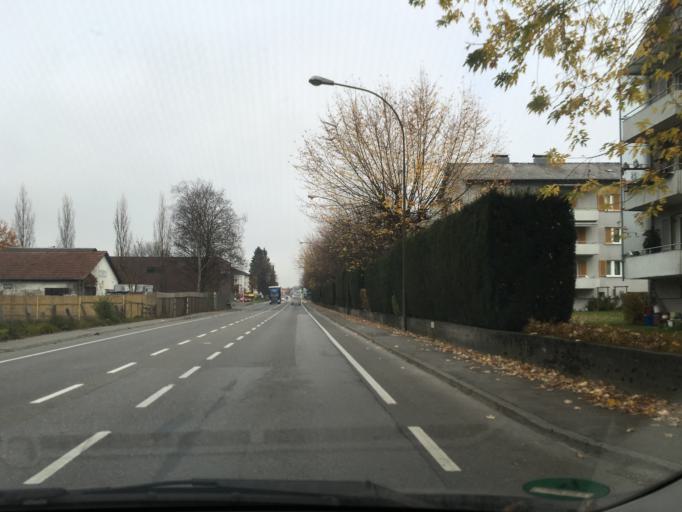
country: AT
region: Vorarlberg
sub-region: Politischer Bezirk Dornbirn
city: Hohenems
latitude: 47.3698
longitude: 9.6736
